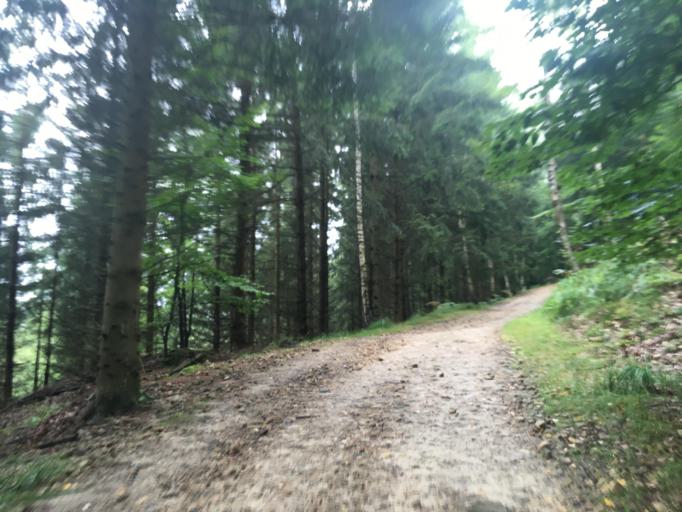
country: DE
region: Saxony
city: Bad Schandau
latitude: 50.9126
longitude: 14.2213
